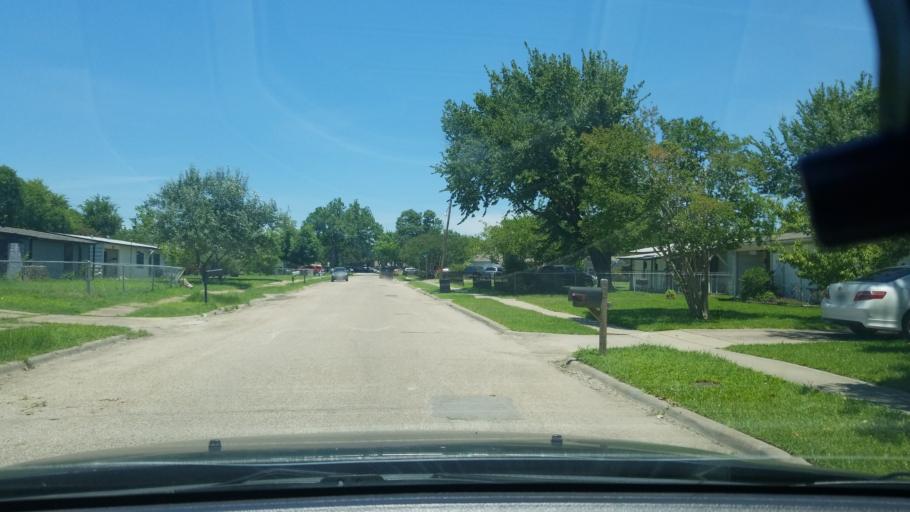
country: US
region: Texas
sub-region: Dallas County
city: Mesquite
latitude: 32.7809
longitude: -96.6045
